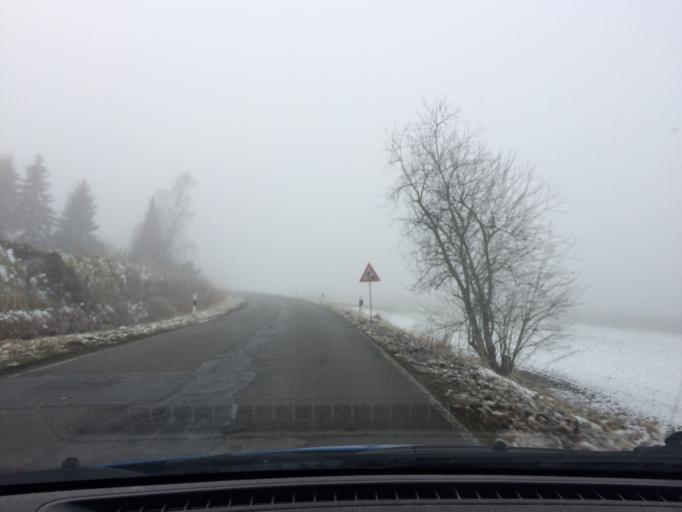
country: DE
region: Schleswig-Holstein
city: Gulzow
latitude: 53.4447
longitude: 10.4877
